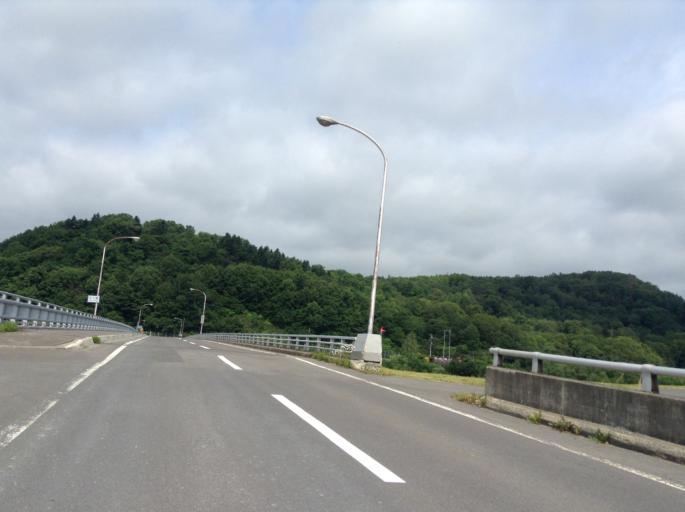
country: JP
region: Hokkaido
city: Nayoro
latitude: 44.7430
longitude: 142.0464
